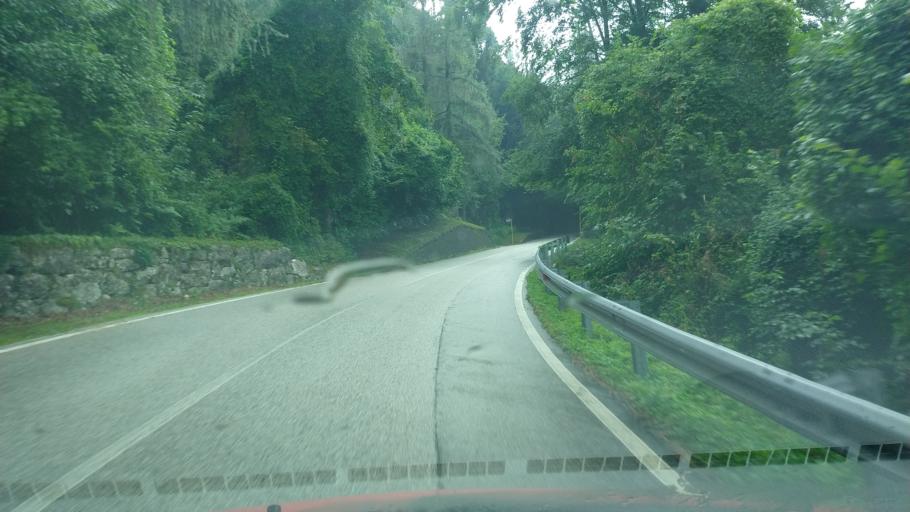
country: IT
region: Veneto
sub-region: Provincia di Vicenza
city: Tonezza del Cimone
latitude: 45.8543
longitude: 11.3537
